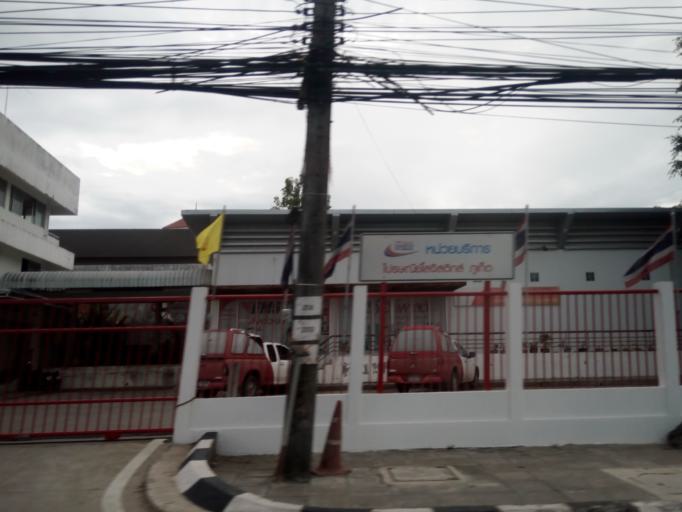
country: TH
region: Phuket
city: Ban Ko Kaeo
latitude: 7.9556
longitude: 98.3880
